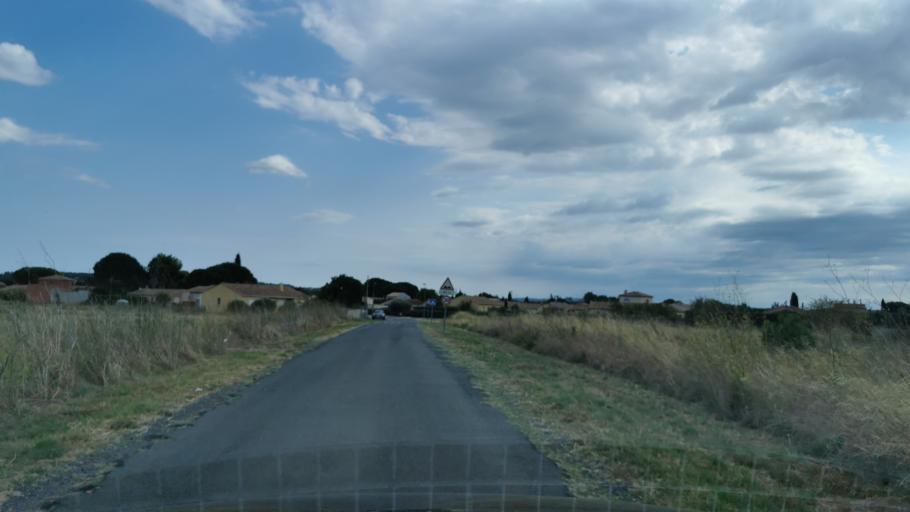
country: FR
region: Languedoc-Roussillon
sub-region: Departement de l'Aude
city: Saint-Marcel-sur-Aude
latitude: 43.2526
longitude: 2.9200
